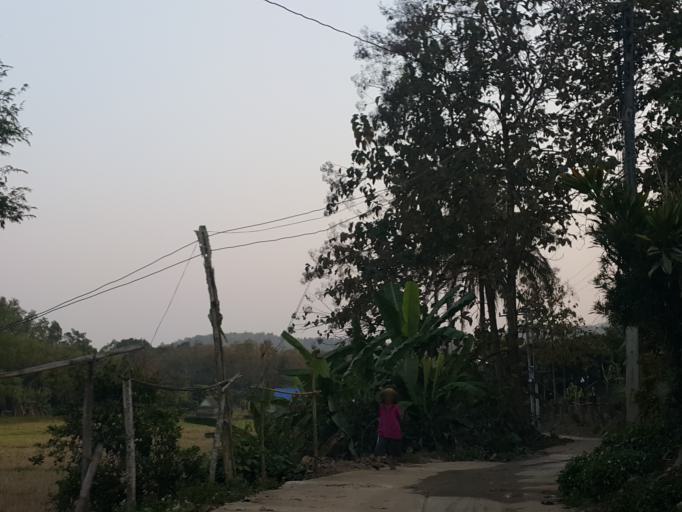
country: TH
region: Chiang Mai
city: Mae Taeng
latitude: 19.1116
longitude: 98.8283
